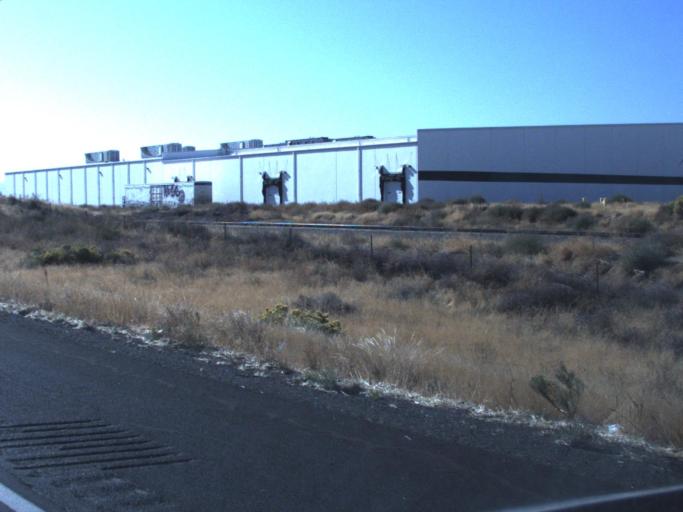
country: US
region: Washington
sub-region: Franklin County
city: Pasco
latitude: 46.2766
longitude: -119.0909
